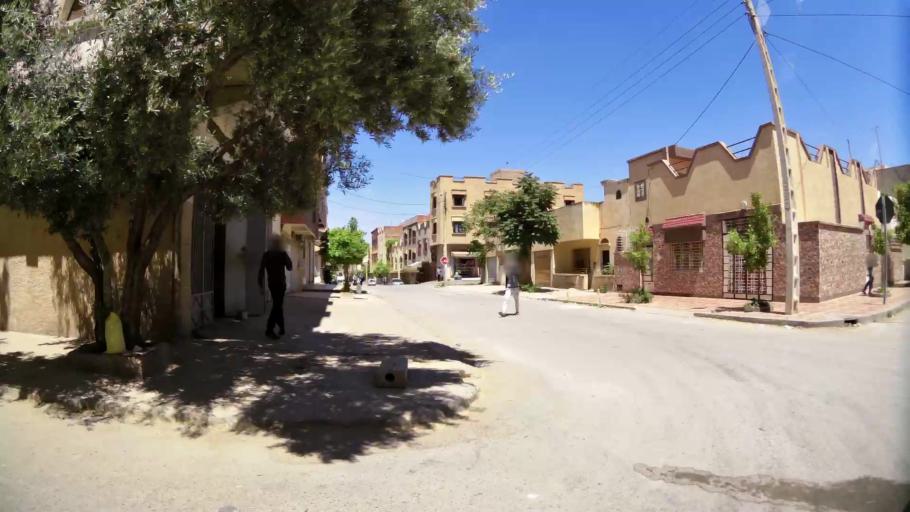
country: MA
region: Oriental
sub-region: Oujda-Angad
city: Oujda
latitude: 34.6590
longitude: -1.9252
